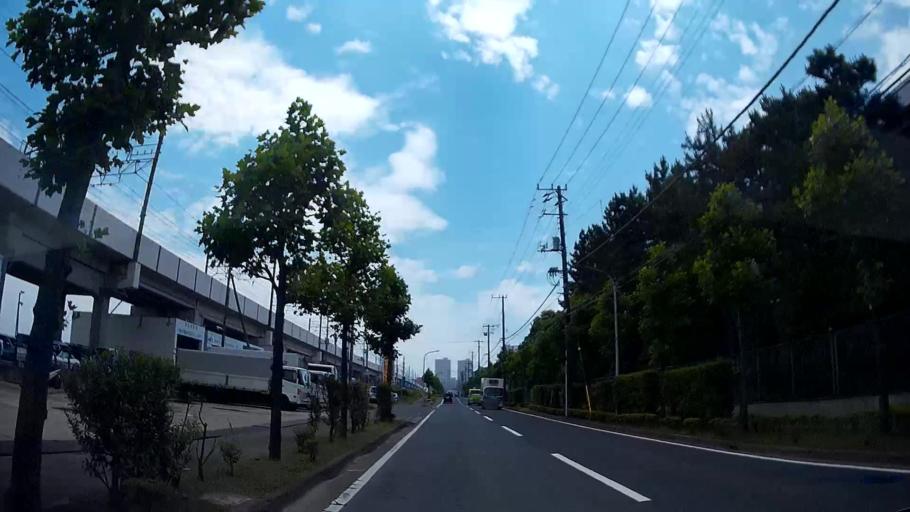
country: JP
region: Tokyo
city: Urayasu
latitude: 35.6607
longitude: 139.9204
